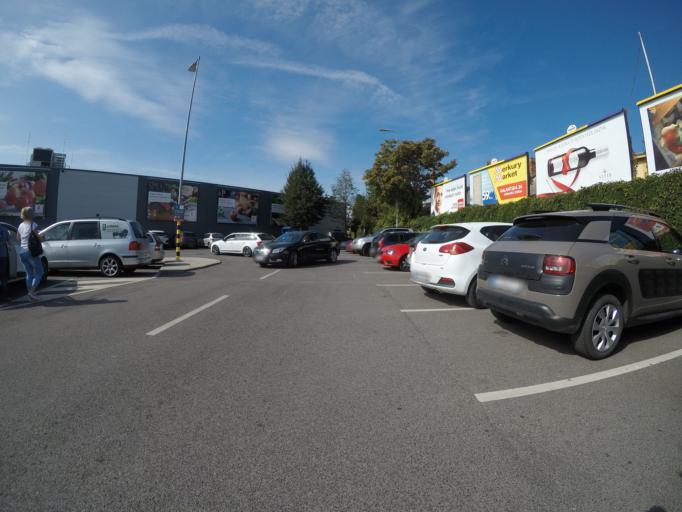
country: SK
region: Trnavsky
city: Dunajska Streda
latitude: 47.9968
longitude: 17.6261
